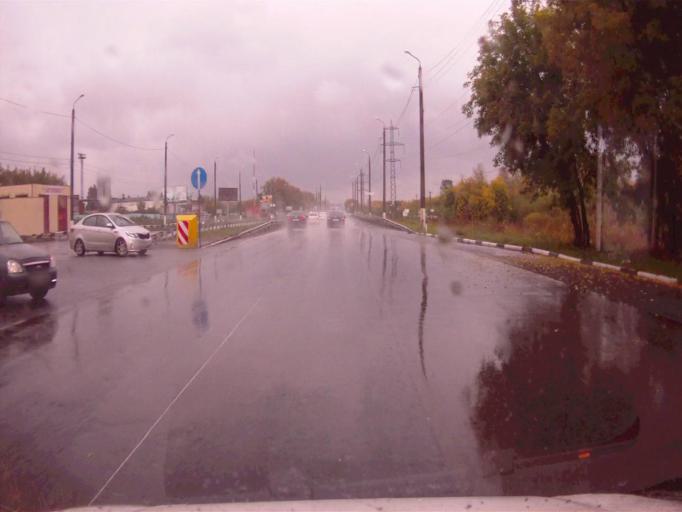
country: RU
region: Chelyabinsk
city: Dolgoderevenskoye
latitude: 55.2528
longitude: 61.3545
